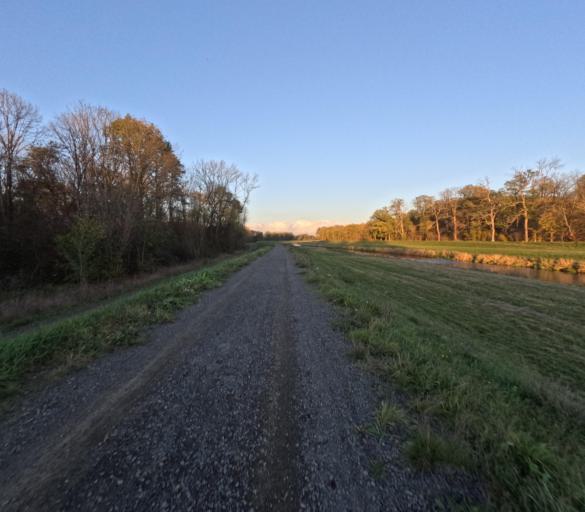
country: DE
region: Saxony
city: Schkeuditz
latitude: 51.3764
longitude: 12.2463
